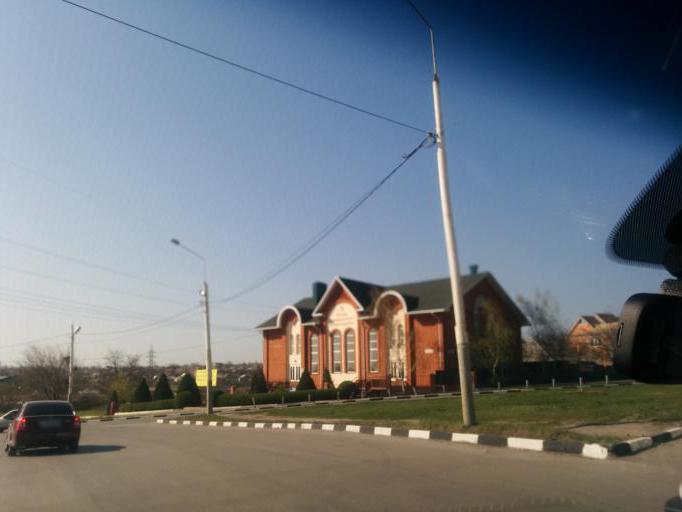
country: RU
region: Rostov
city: Shakhty
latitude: 47.7095
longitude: 40.1816
